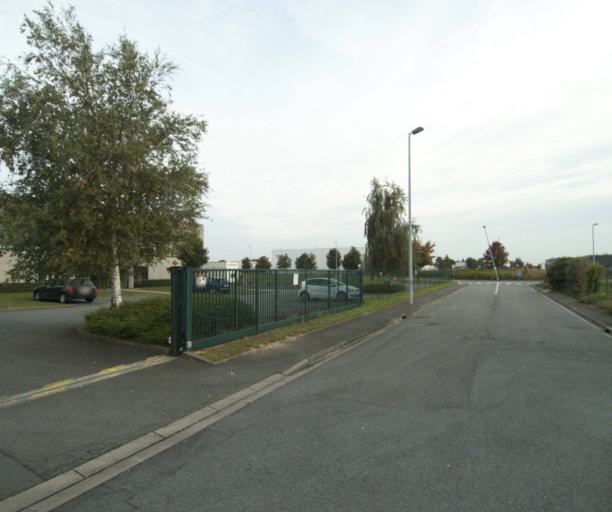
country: FR
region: Nord-Pas-de-Calais
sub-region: Departement du Nord
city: Templemars
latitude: 50.5589
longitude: 3.0587
